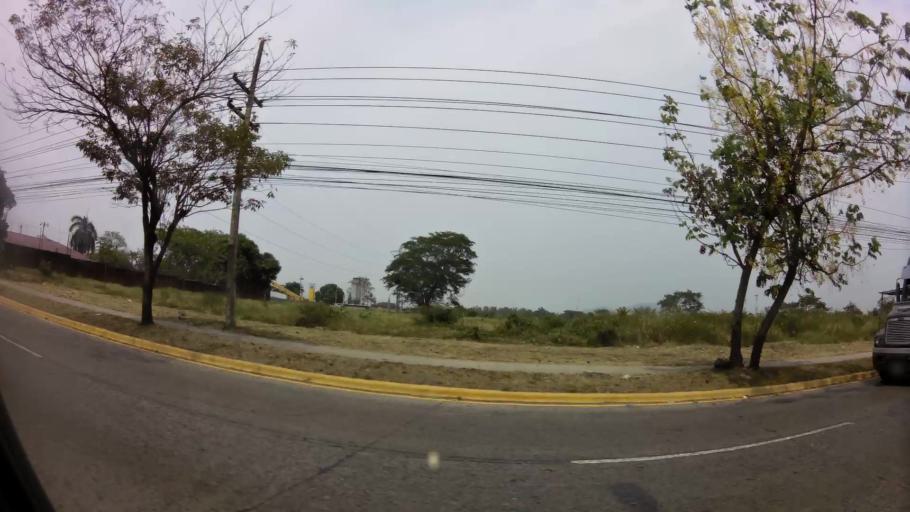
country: HN
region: Cortes
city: Armenta
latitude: 15.4748
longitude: -88.0338
